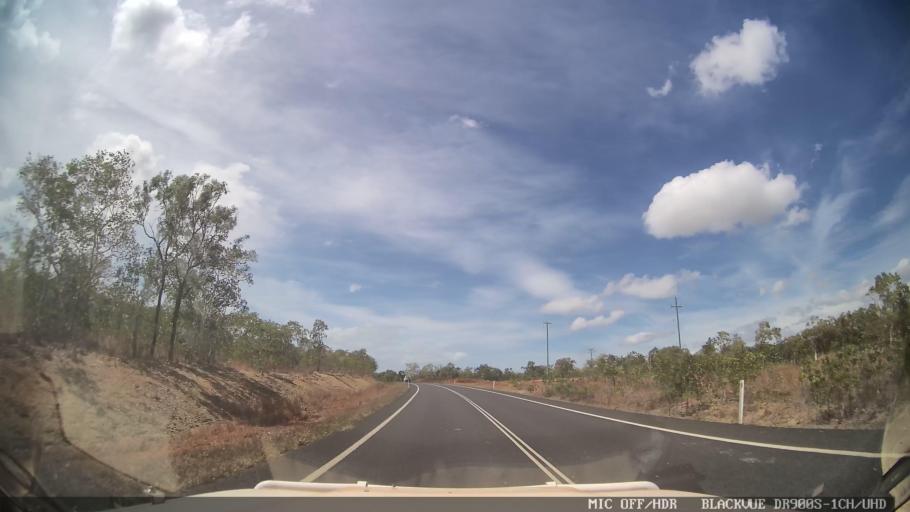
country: AU
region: Queensland
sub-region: Cook
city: Cooktown
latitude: -15.5342
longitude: 145.2320
